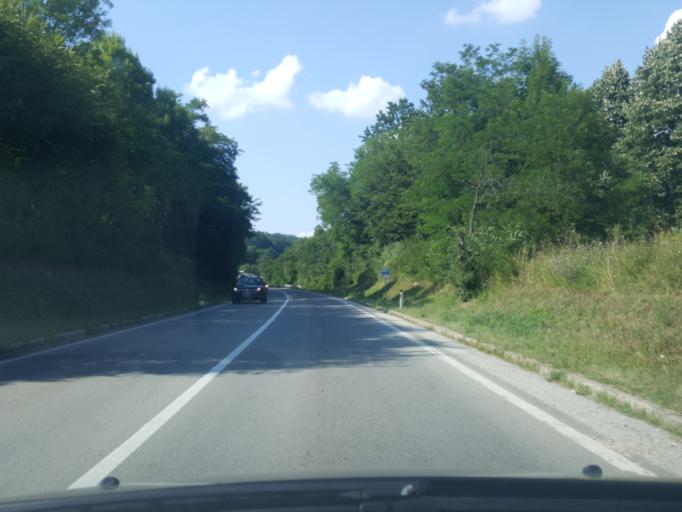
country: RS
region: Central Serbia
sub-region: Moravicki Okrug
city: Gornji Milanovac
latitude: 44.0963
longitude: 20.4812
